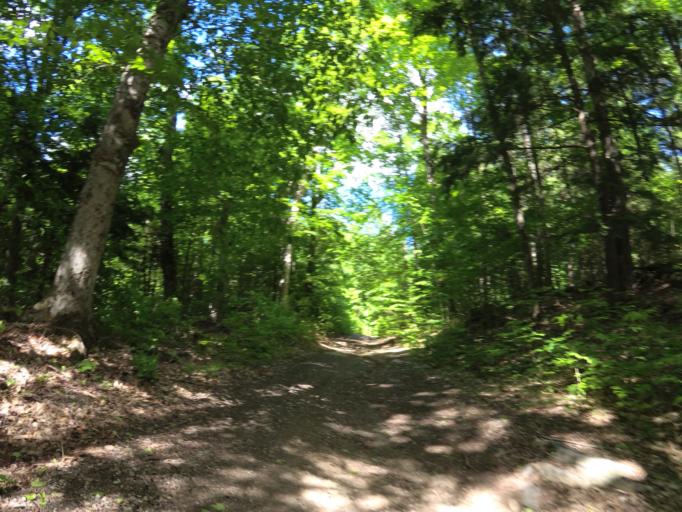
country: CA
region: Ontario
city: Renfrew
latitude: 45.0435
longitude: -76.8391
